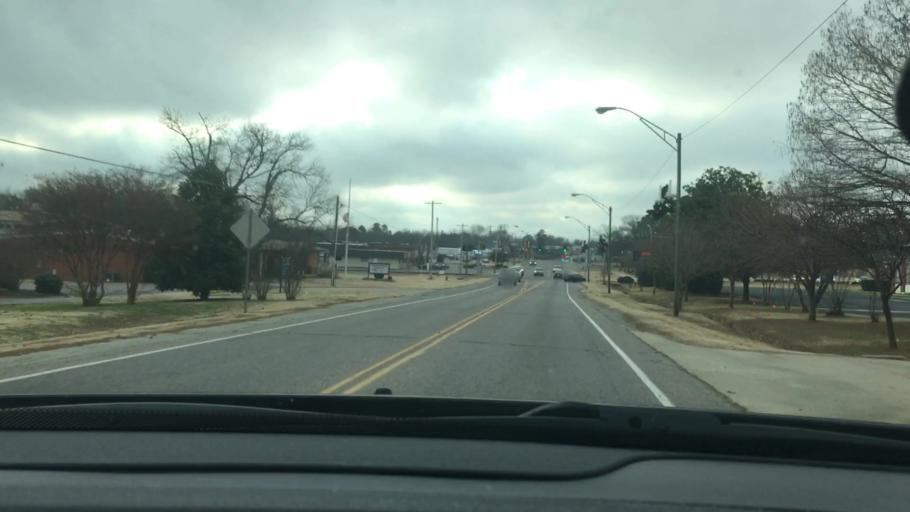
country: US
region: Oklahoma
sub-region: Bryan County
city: Durant
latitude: 34.0065
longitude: -96.3730
